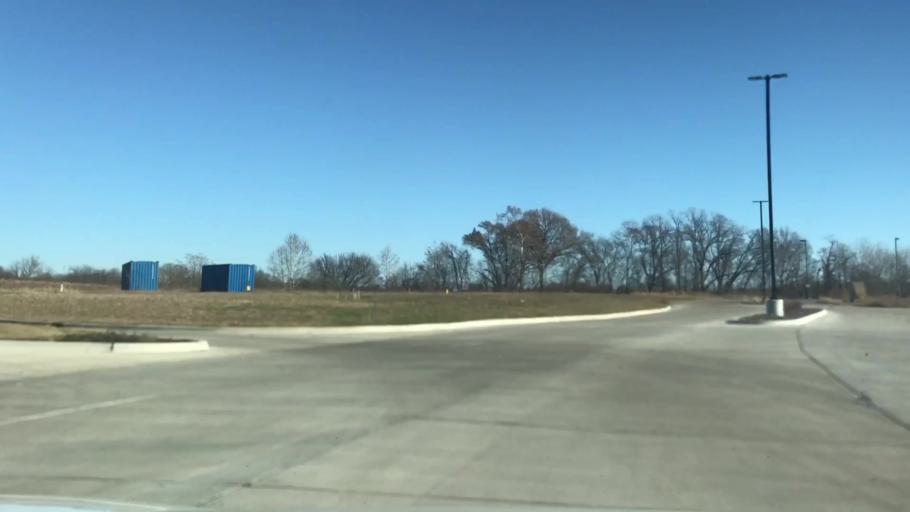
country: US
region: Illinois
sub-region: Saint Clair County
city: Alorton
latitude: 38.5622
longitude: -90.0834
